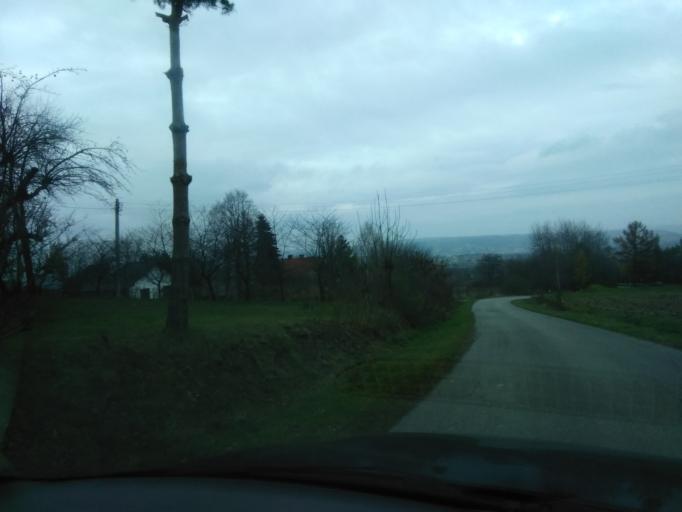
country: PL
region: Subcarpathian Voivodeship
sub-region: Powiat strzyzowski
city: Wysoka Strzyzowska
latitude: 49.8332
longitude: 21.7749
